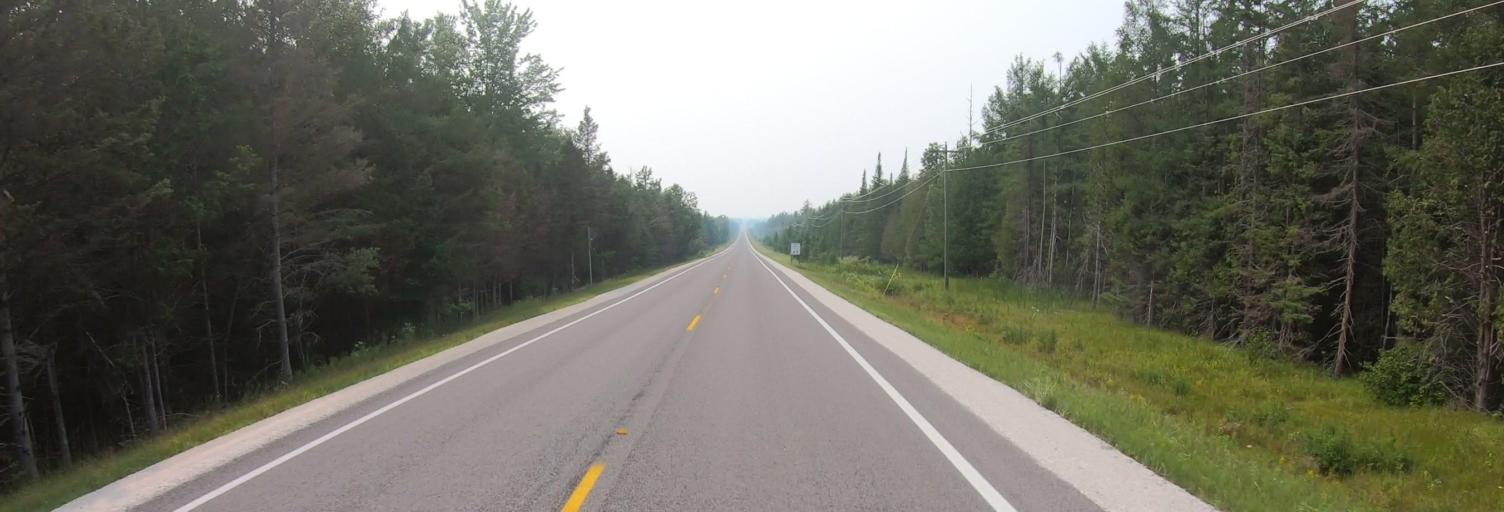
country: US
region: Michigan
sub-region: Chippewa County
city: Sault Ste. Marie
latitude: 46.0720
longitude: -84.1788
